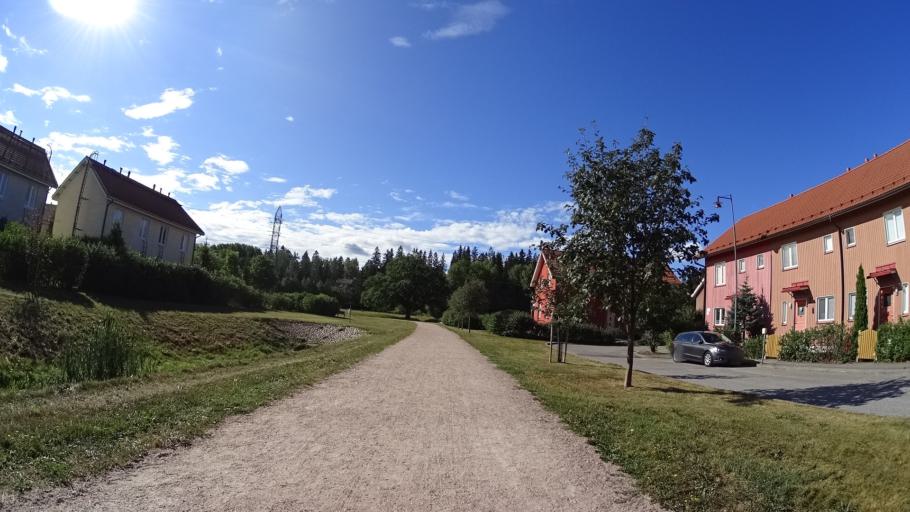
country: FI
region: Uusimaa
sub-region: Helsinki
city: Vantaa
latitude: 60.2801
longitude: 24.9664
